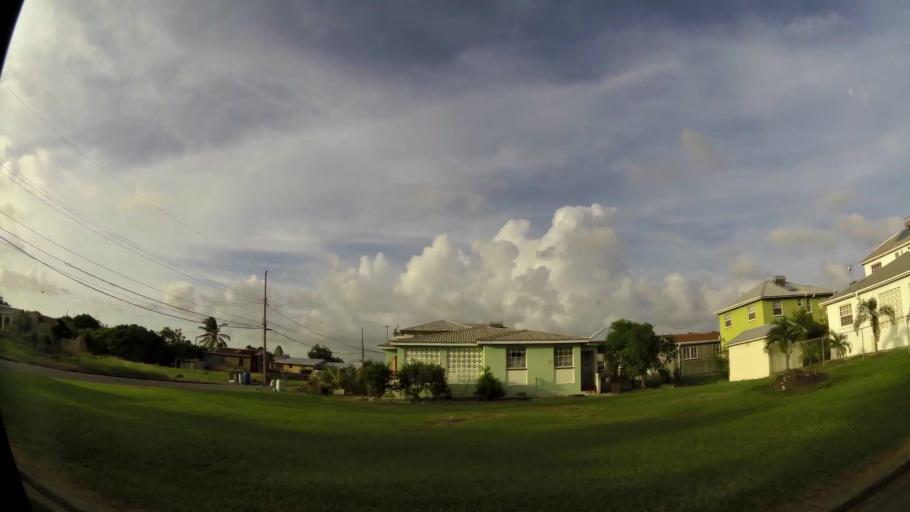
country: BB
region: Christ Church
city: Oistins
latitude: 13.0559
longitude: -59.5133
